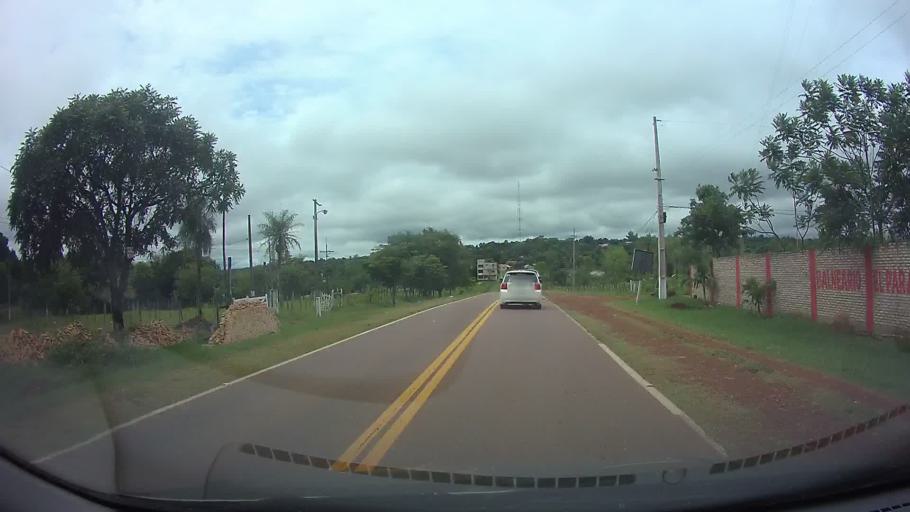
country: PY
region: Paraguari
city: Acahay
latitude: -25.9029
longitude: -57.1161
